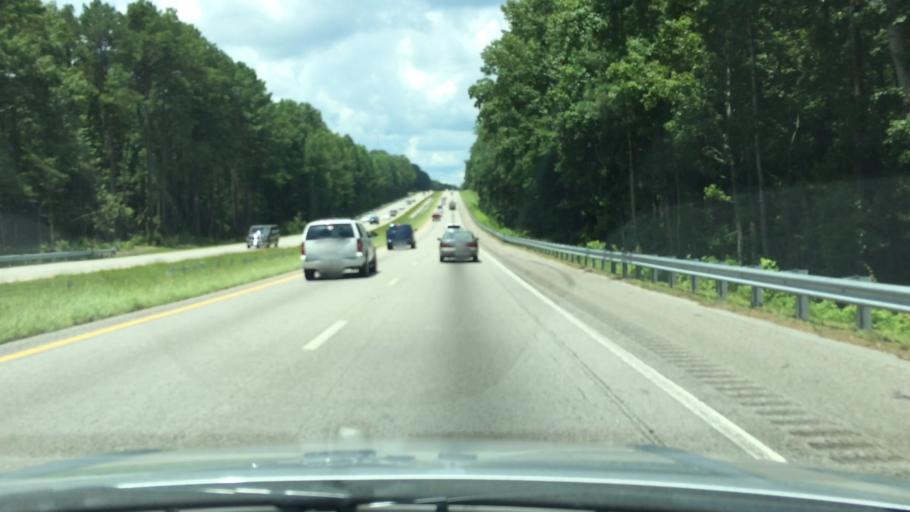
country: US
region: South Carolina
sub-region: Laurens County
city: Joanna
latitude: 34.4575
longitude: -81.7902
